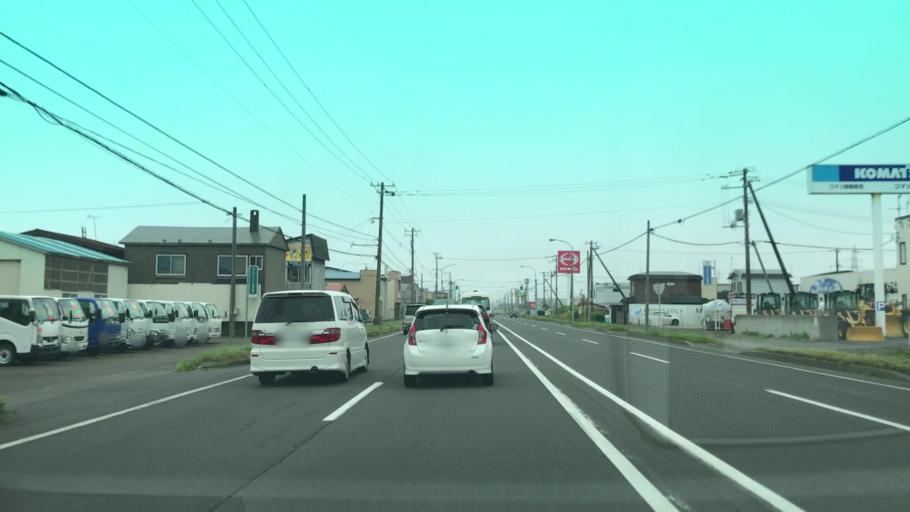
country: JP
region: Hokkaido
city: Muroran
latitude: 42.3742
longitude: 141.0670
